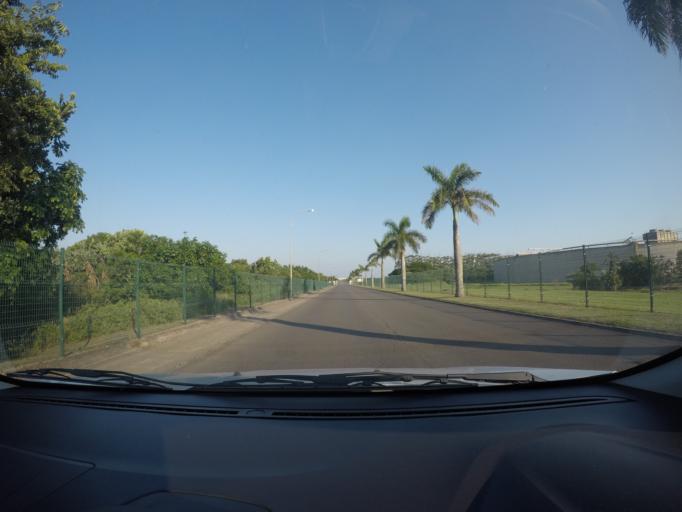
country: ZA
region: KwaZulu-Natal
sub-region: uThungulu District Municipality
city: Richards Bay
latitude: -28.7644
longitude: 31.9974
